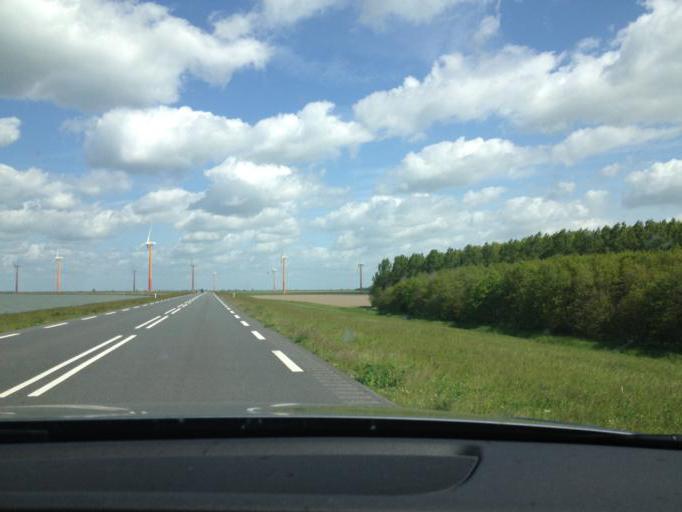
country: NL
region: North Holland
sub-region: Gemeente Naarden
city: Naarden
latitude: 52.3606
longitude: 5.1324
